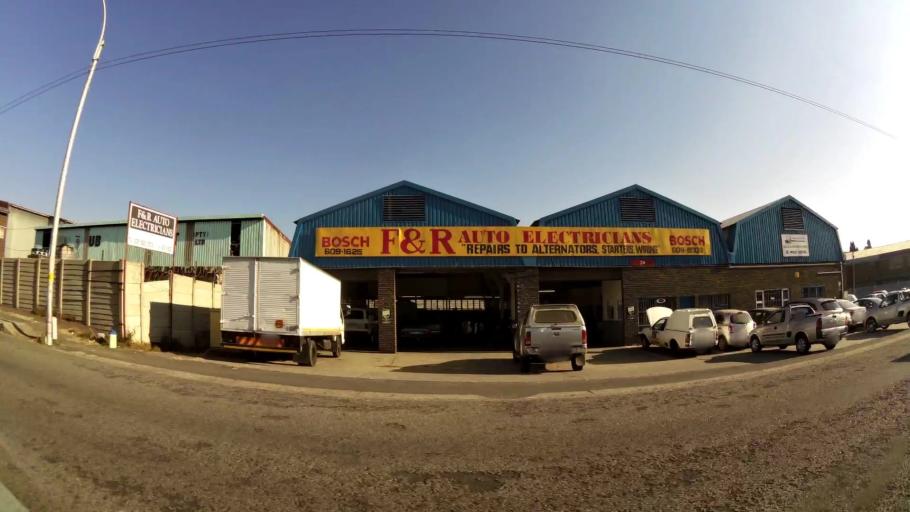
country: ZA
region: Gauteng
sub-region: City of Johannesburg Metropolitan Municipality
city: Modderfontein
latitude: -26.1320
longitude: 28.1582
